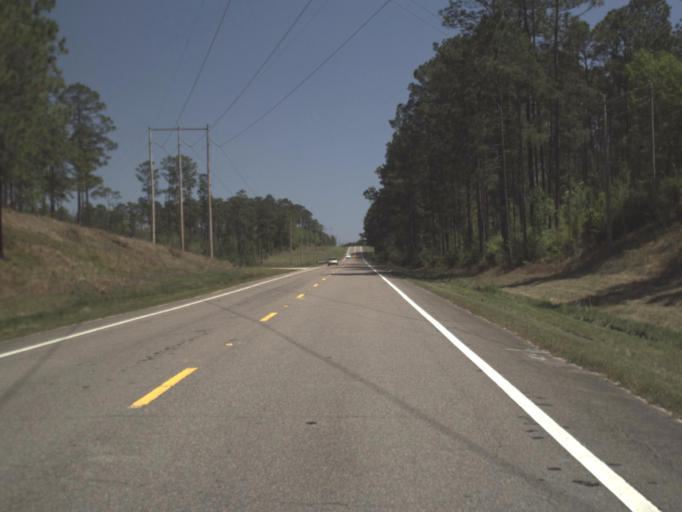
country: US
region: Florida
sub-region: Santa Rosa County
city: Point Baker
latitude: 30.8804
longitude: -86.9539
